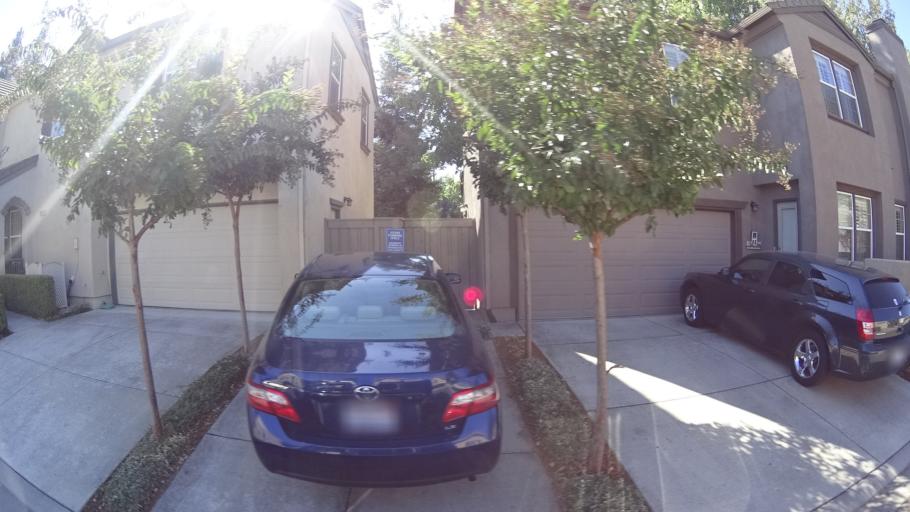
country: US
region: California
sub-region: Sacramento County
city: Parkway
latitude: 38.4770
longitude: -121.5289
